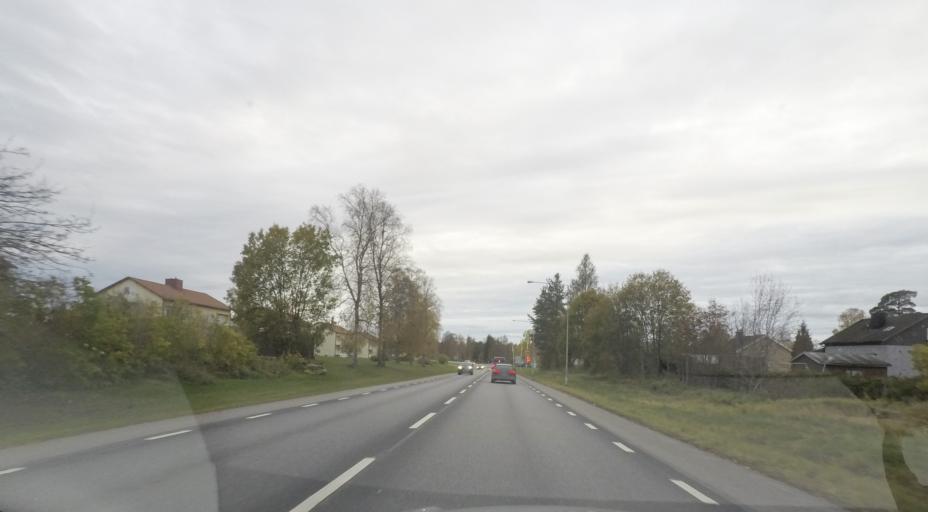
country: SE
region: OErebro
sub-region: Hallefors Kommun
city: Haellefors
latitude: 59.7781
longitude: 14.5268
